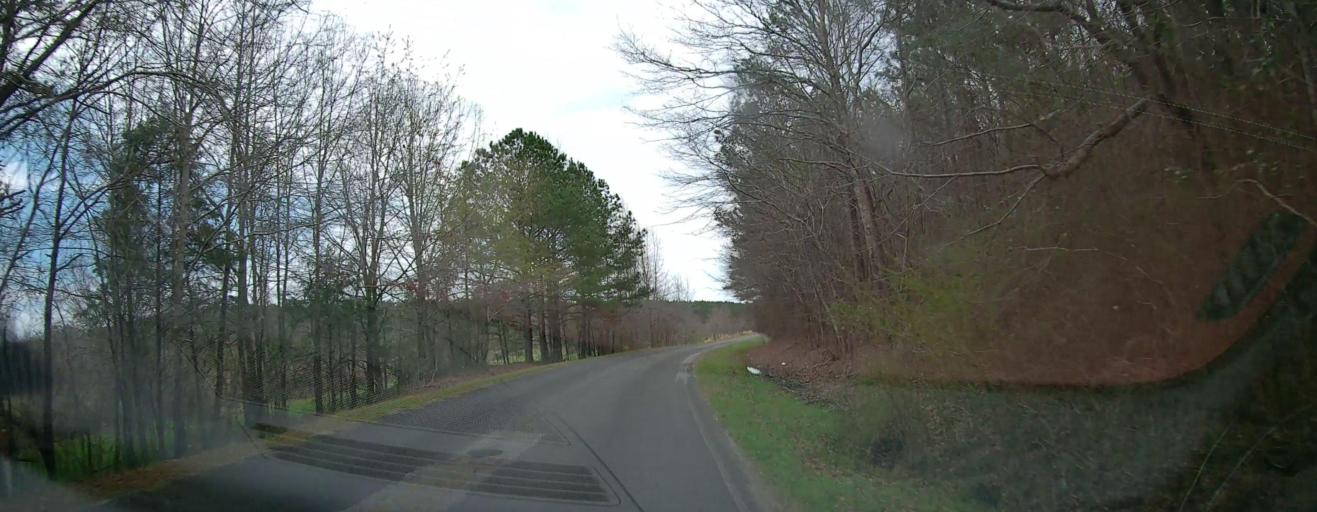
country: US
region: Alabama
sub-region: Marion County
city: Hamilton
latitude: 34.2005
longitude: -88.1713
